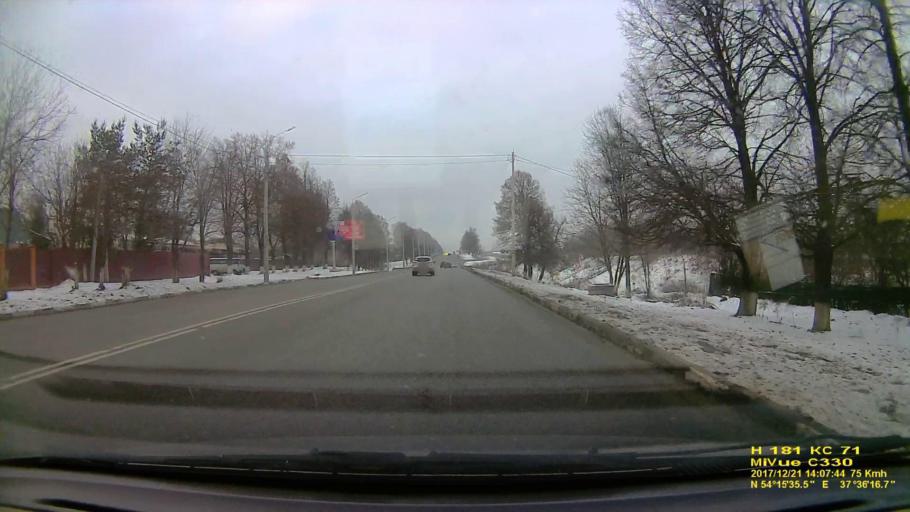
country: RU
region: Tula
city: Gorelki
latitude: 54.2601
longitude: 37.6045
